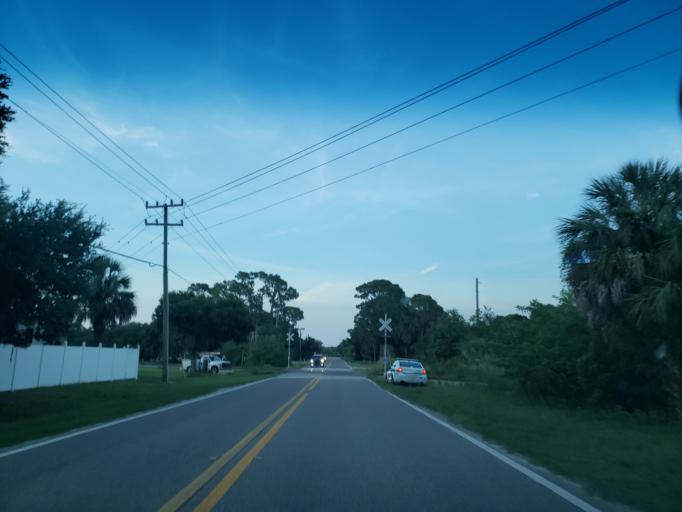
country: US
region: Florida
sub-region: Manatee County
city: Memphis
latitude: 27.5925
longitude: -82.5438
